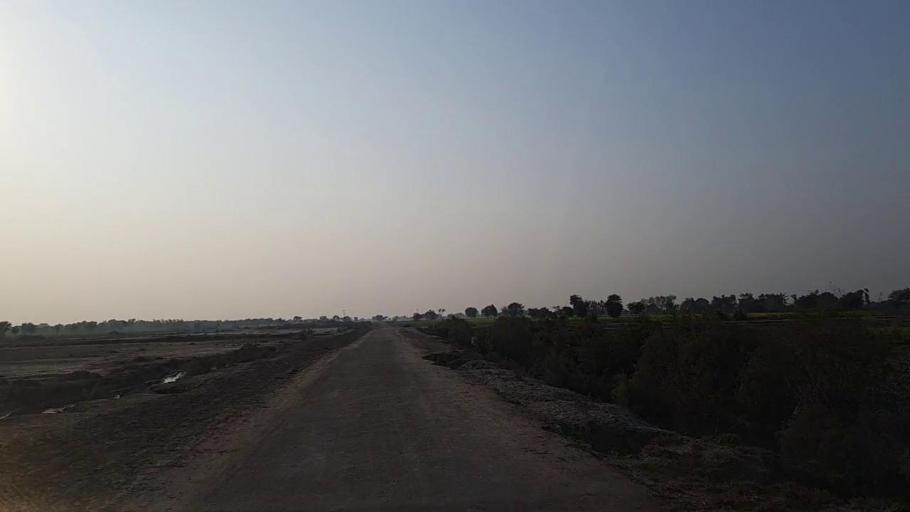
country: PK
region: Sindh
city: Daur
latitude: 26.4071
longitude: 68.3899
